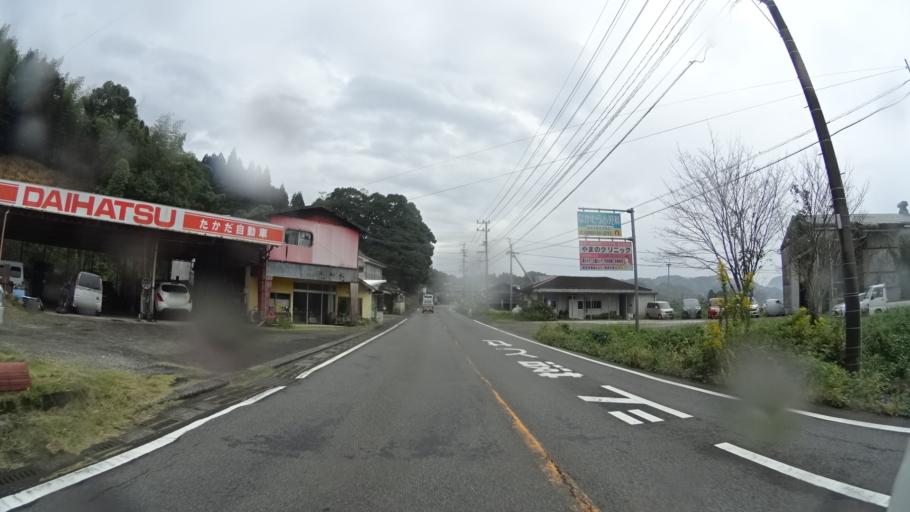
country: JP
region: Kagoshima
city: Kajiki
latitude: 31.7586
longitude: 130.6750
